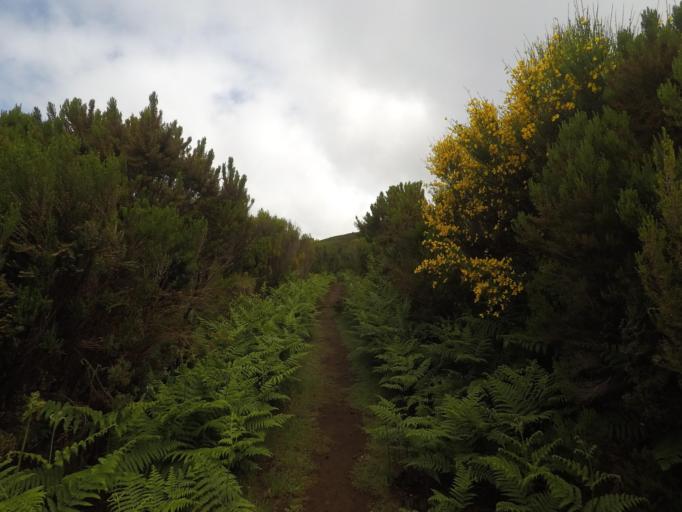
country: PT
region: Madeira
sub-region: Calheta
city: Arco da Calheta
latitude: 32.7761
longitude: -17.1334
